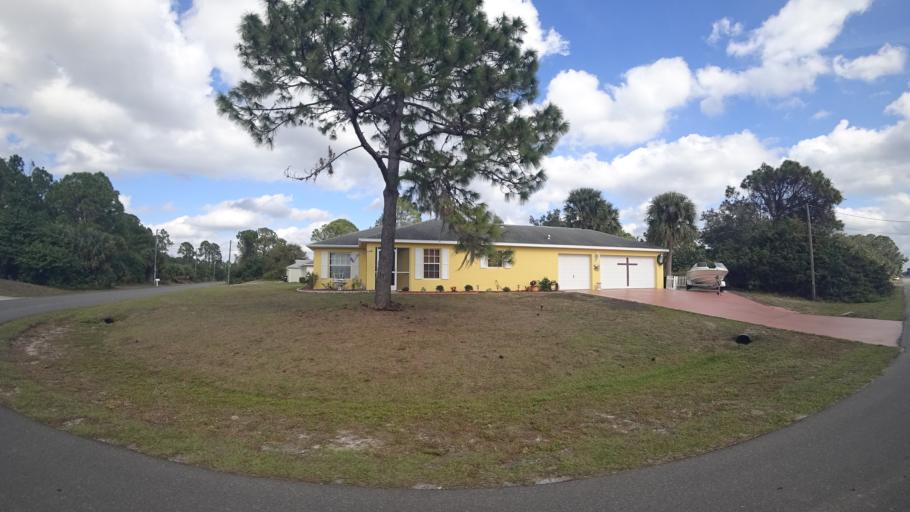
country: US
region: Florida
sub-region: Charlotte County
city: Port Charlotte
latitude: 27.0340
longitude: -82.1383
